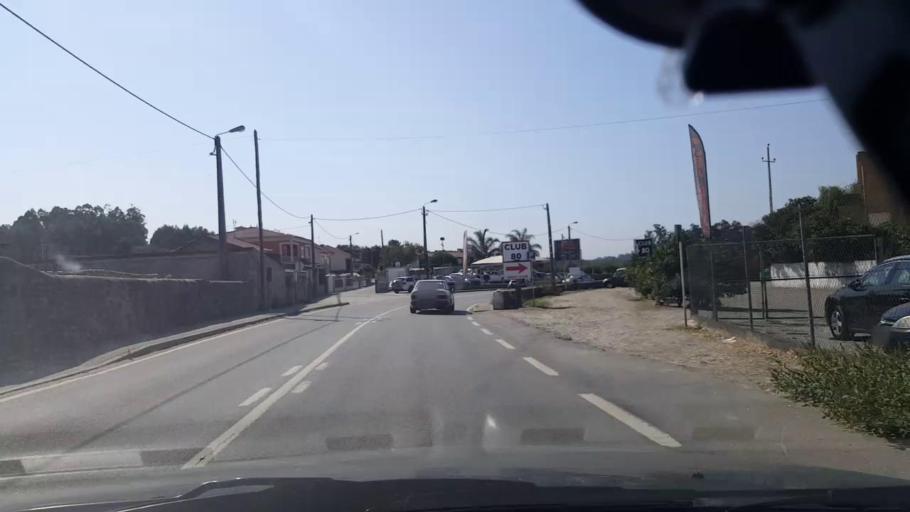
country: PT
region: Porto
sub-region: Povoa de Varzim
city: Pedroso
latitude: 41.3990
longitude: -8.6836
